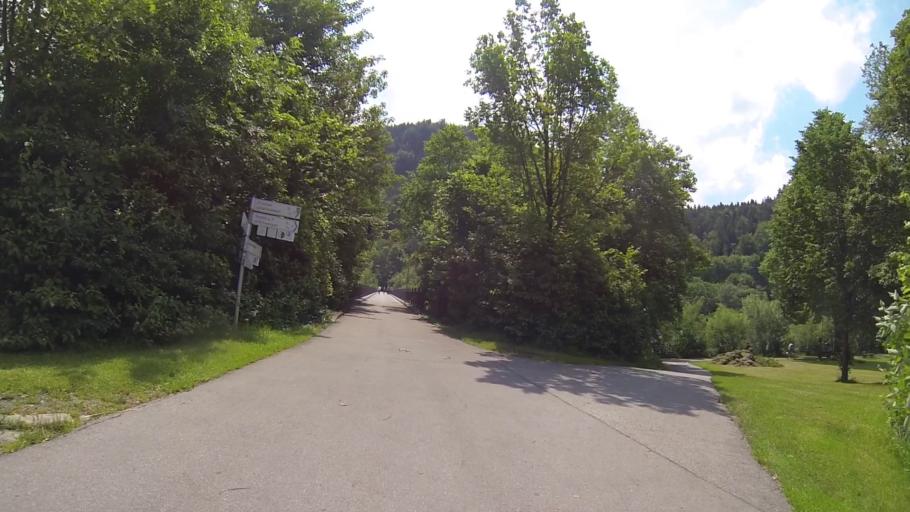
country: DE
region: Bavaria
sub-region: Swabia
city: Fuessen
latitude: 47.5668
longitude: 10.7083
